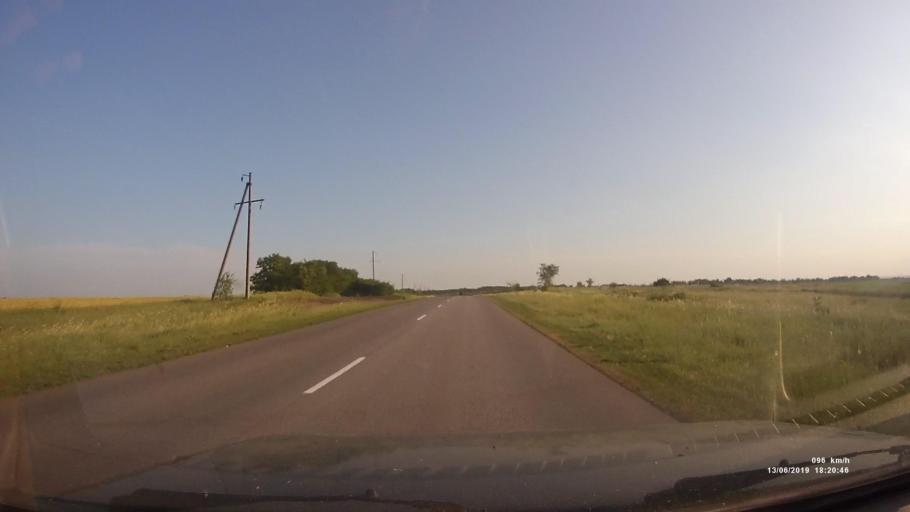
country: RU
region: Rostov
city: Kazanskaya
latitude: 49.8794
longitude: 41.2966
